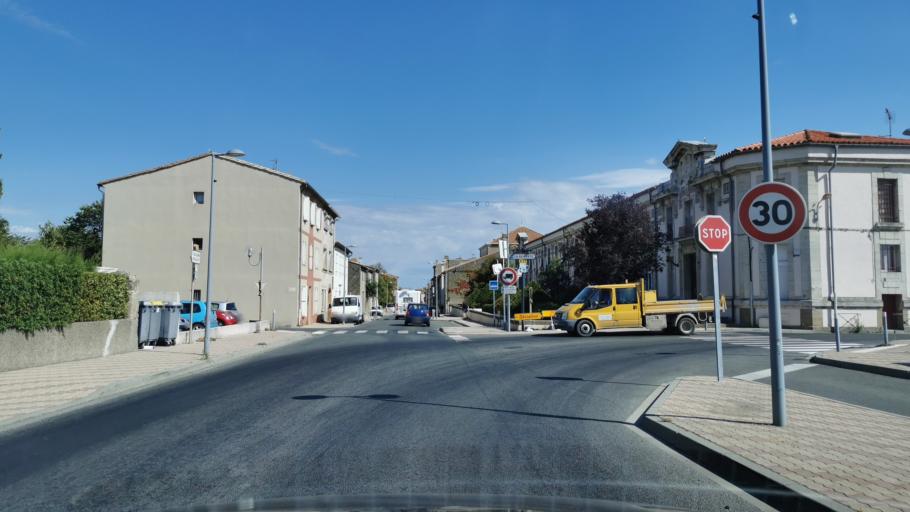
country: FR
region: Languedoc-Roussillon
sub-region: Departement de l'Aude
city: Rieux-Minervois
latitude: 43.2832
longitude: 2.5805
